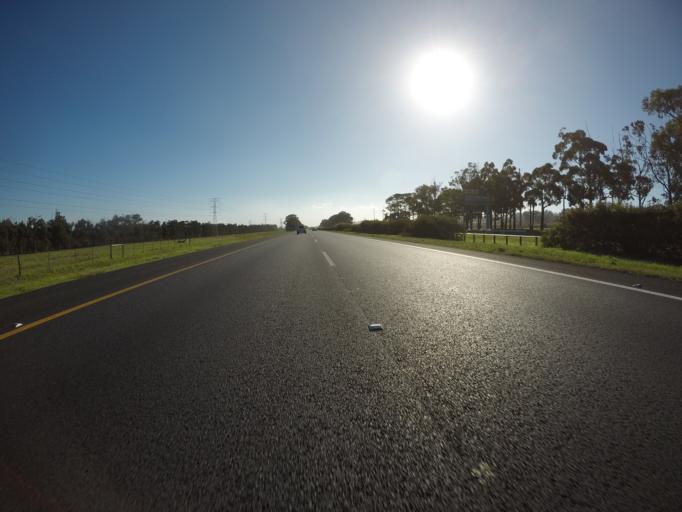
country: ZA
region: Western Cape
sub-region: Cape Winelands District Municipality
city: Stellenbosch
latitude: -34.0658
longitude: 18.8058
